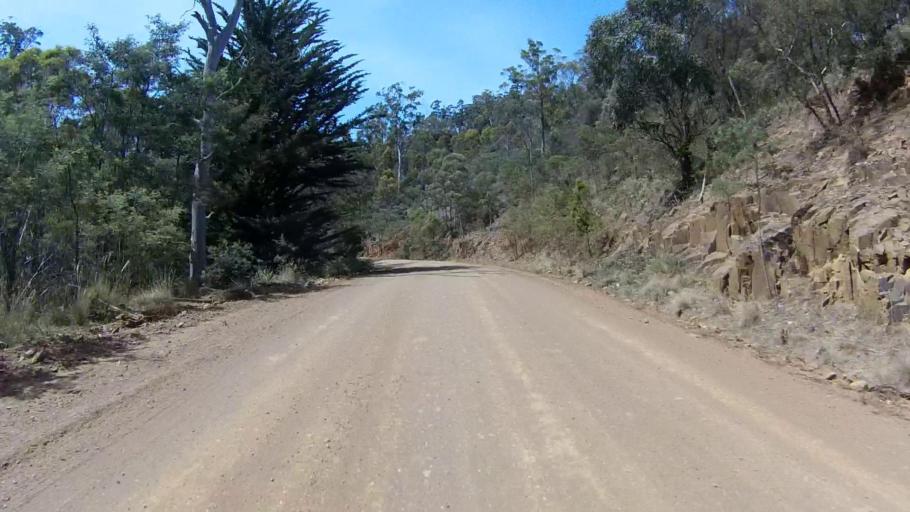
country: AU
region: Tasmania
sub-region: Sorell
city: Sorell
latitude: -42.6415
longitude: 147.7351
